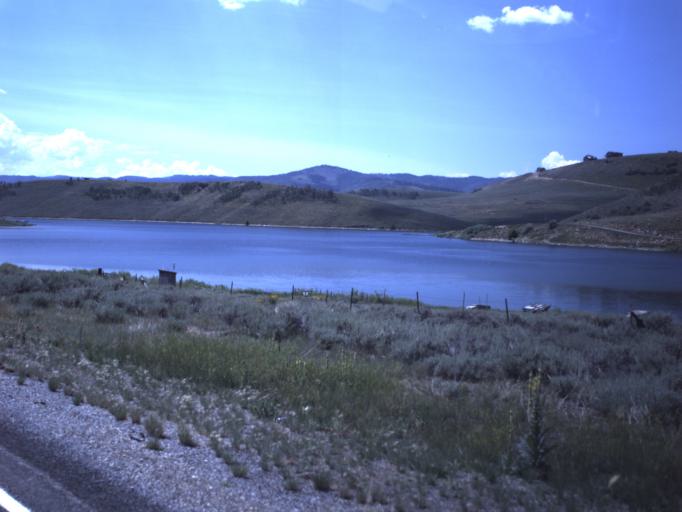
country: US
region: Utah
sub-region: Carbon County
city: Helper
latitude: 39.8109
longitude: -111.1352
